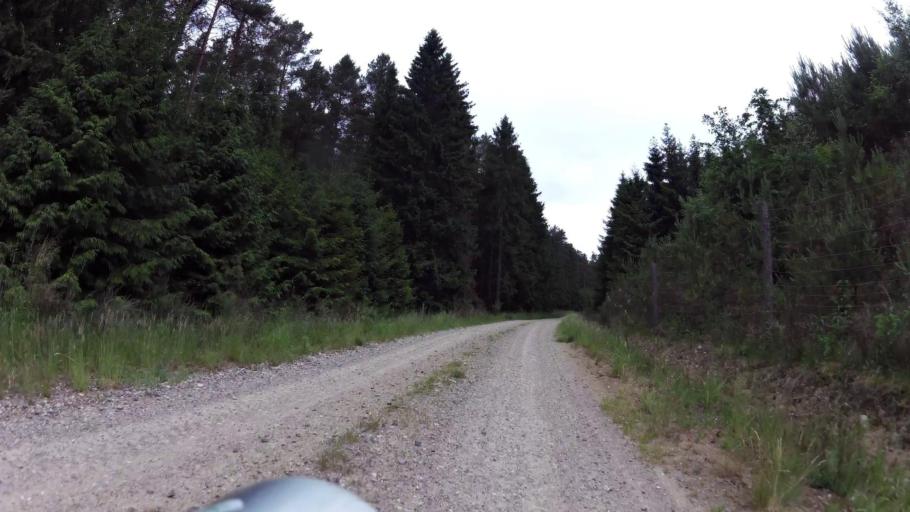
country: PL
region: West Pomeranian Voivodeship
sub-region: Powiat szczecinecki
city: Bialy Bor
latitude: 53.9487
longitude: 16.8288
